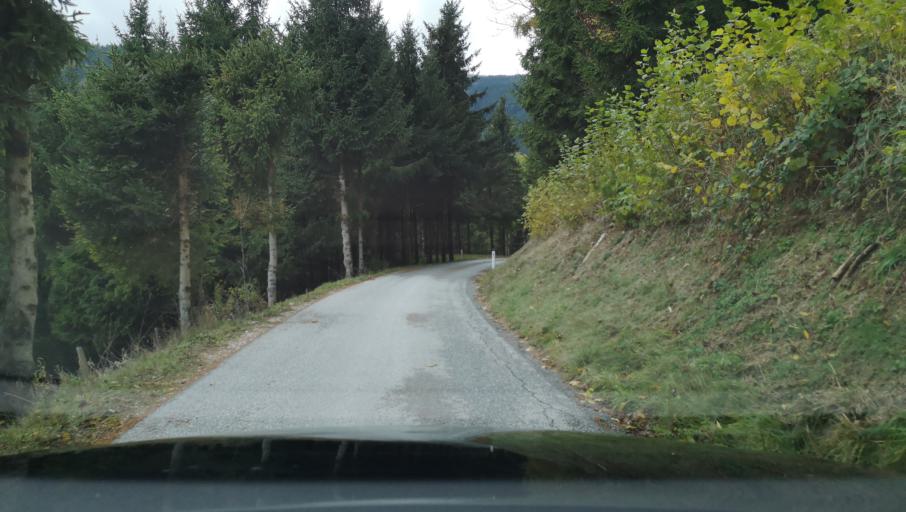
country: AT
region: Styria
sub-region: Politischer Bezirk Weiz
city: Birkfeld
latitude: 47.3675
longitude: 15.6349
